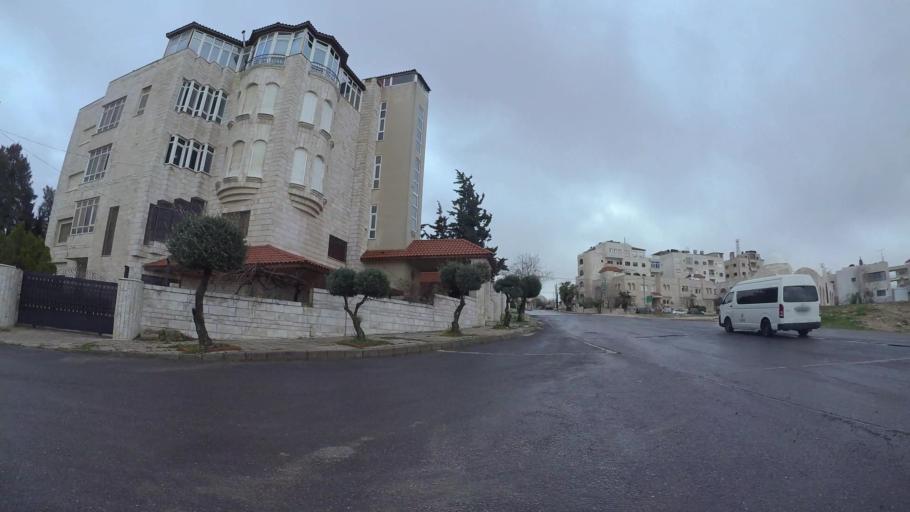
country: JO
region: Amman
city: Al Jubayhah
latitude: 32.0319
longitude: 35.8545
